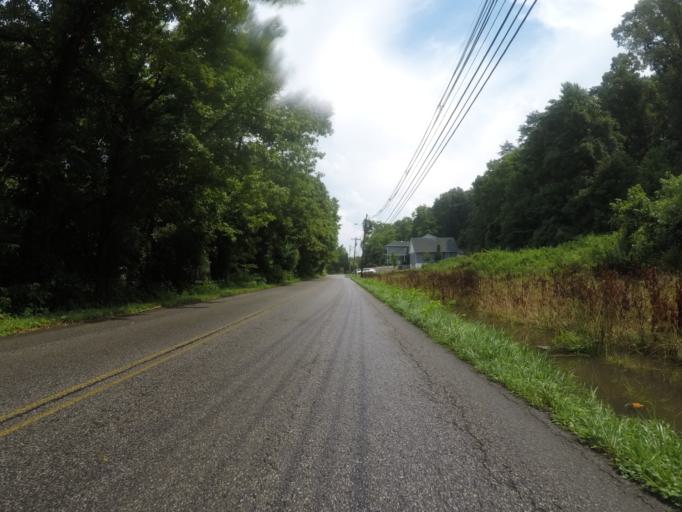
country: US
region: Kentucky
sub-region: Boyd County
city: Westwood
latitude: 38.4720
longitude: -82.6707
